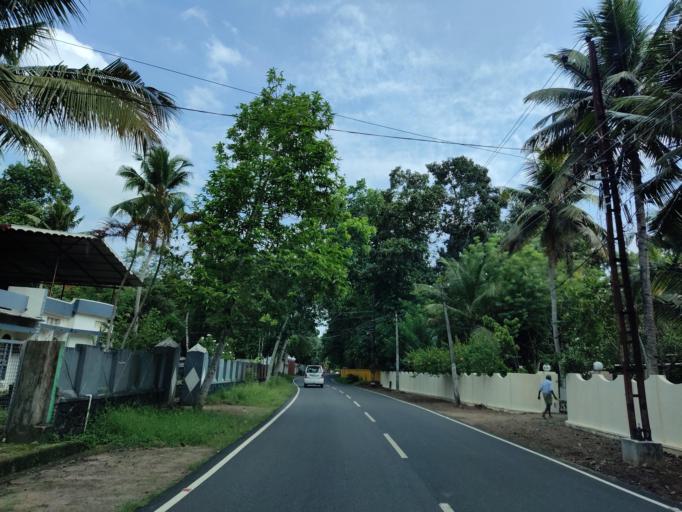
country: IN
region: Kerala
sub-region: Alappuzha
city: Mavelikara
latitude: 9.2637
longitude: 76.5592
